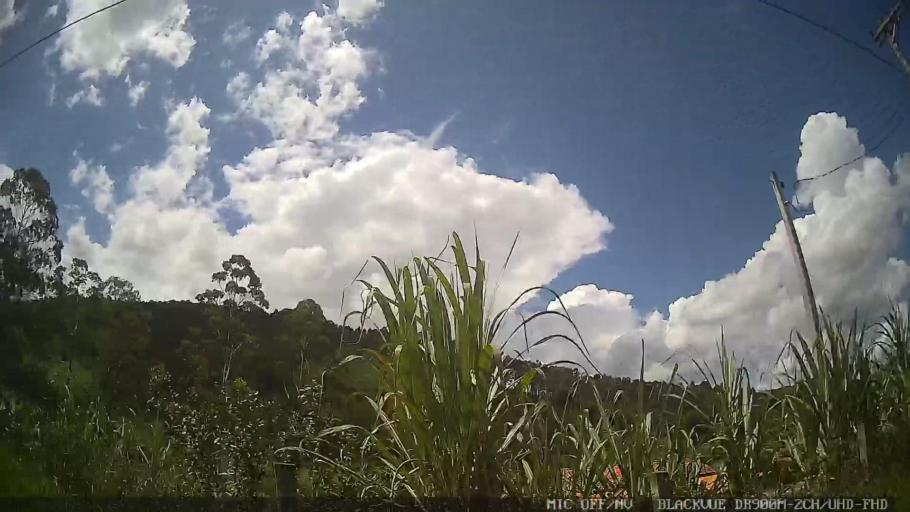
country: BR
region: Sao Paulo
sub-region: Caraguatatuba
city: Caraguatatuba
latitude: -23.5341
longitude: -45.5620
